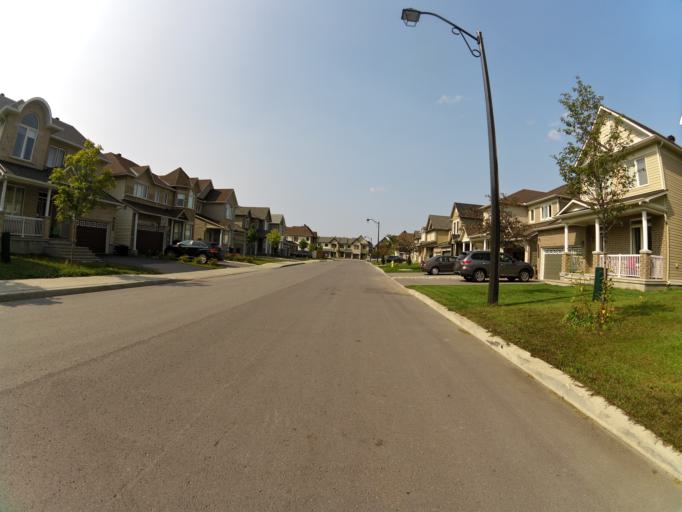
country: CA
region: Ontario
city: Bells Corners
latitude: 45.3032
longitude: -75.9343
